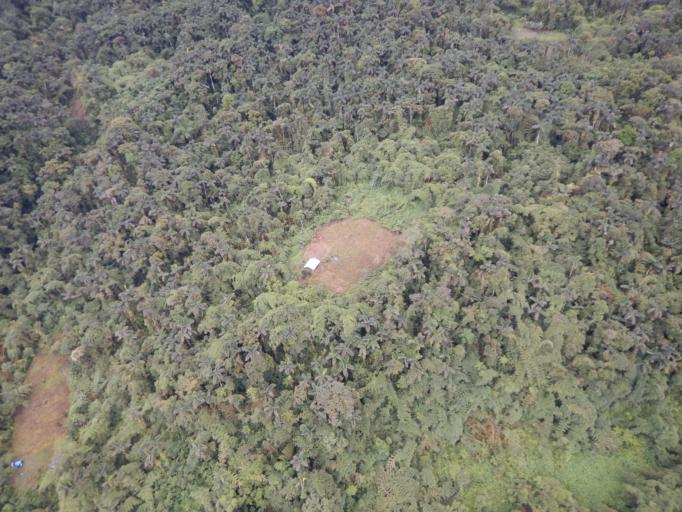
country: BO
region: Cochabamba
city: Totora
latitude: -17.3960
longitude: -65.2437
